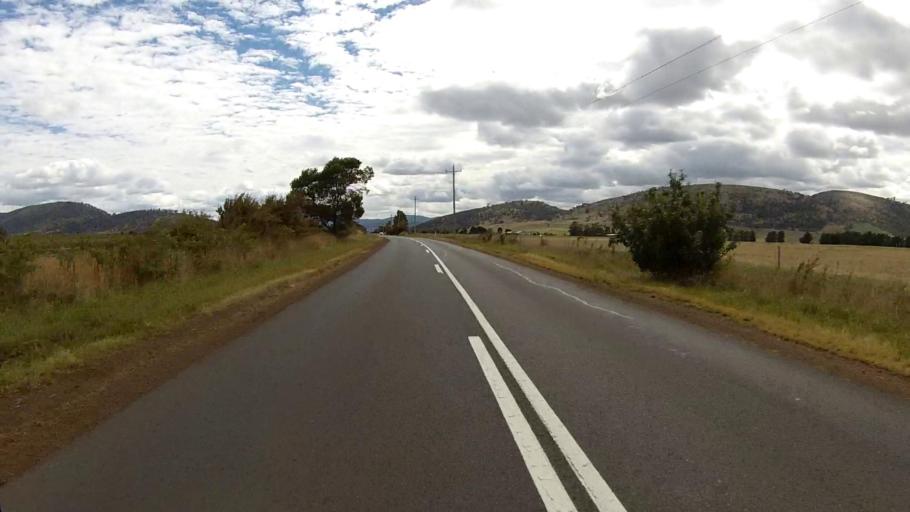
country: AU
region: Tasmania
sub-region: Clarence
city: Cambridge
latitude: -42.7586
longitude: 147.4030
